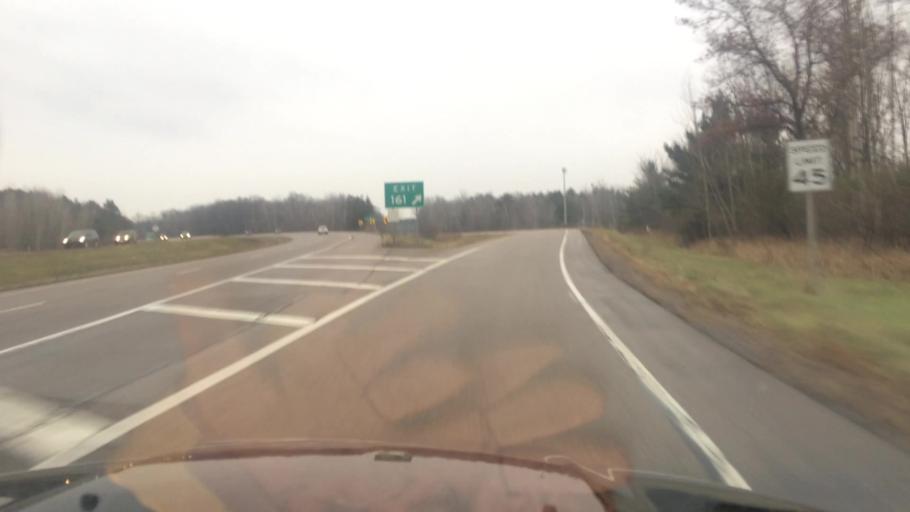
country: US
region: Wisconsin
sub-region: Portage County
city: Stevens Point
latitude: 44.5519
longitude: -89.5837
